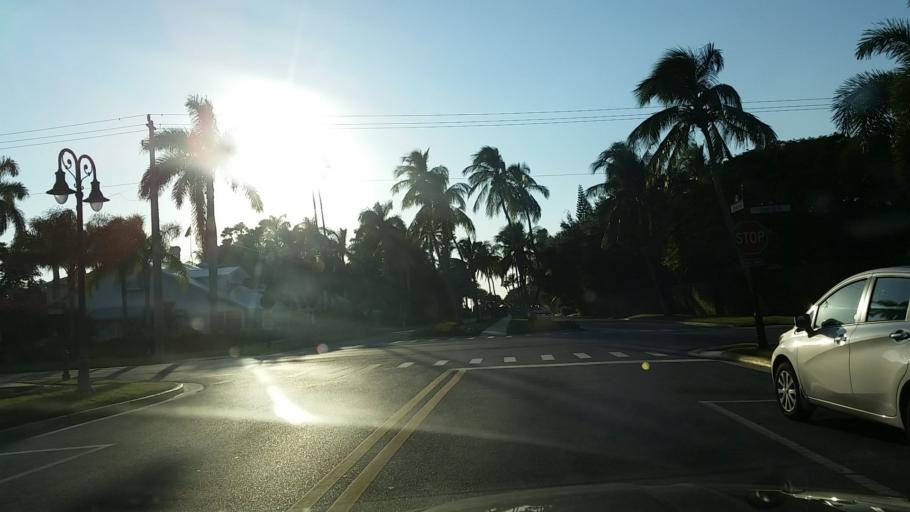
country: US
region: Florida
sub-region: Collier County
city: Naples
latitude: 26.1332
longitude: -81.8031
